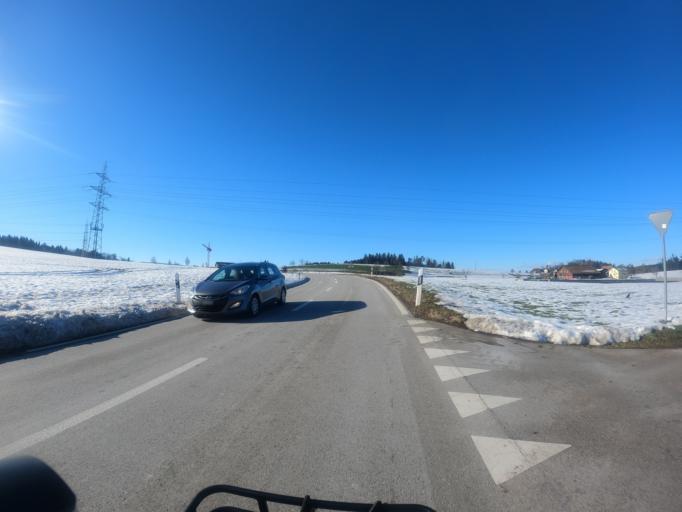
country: CH
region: Zurich
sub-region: Bezirk Affoltern
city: Ottenbach
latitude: 47.2897
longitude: 8.4265
